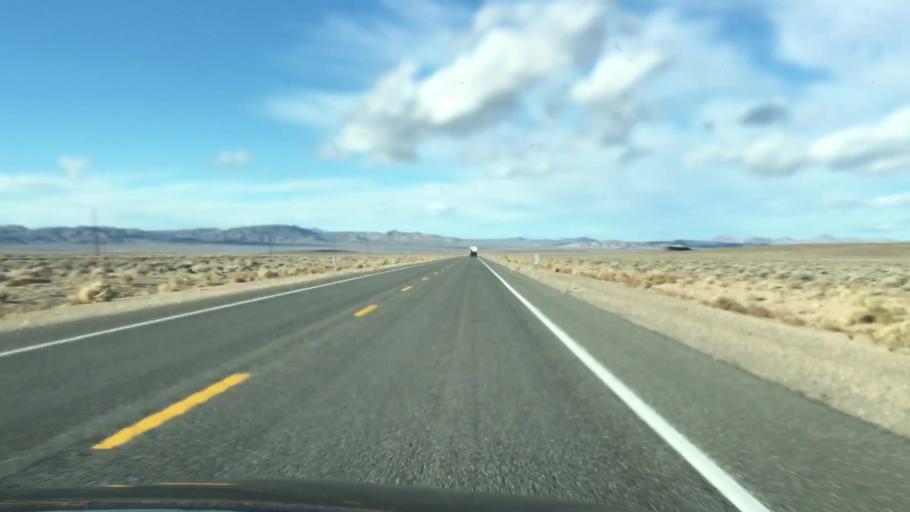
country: US
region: Nevada
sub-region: Esmeralda County
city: Goldfield
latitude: 37.4121
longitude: -117.1533
